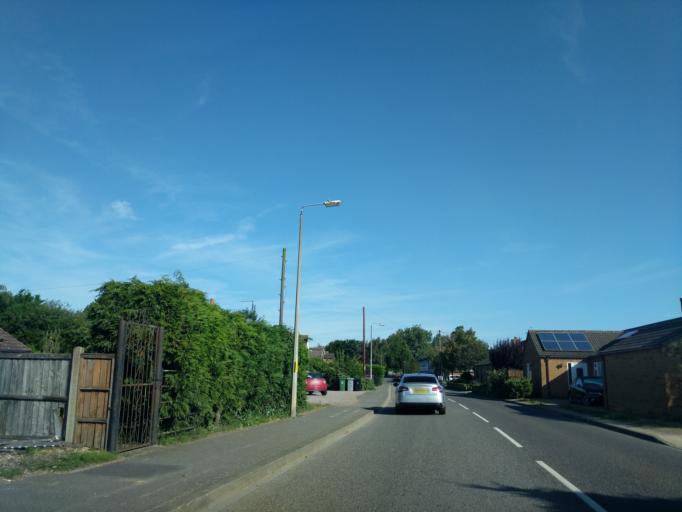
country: GB
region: England
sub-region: Lincolnshire
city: Bourne
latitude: 52.7661
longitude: -0.3626
